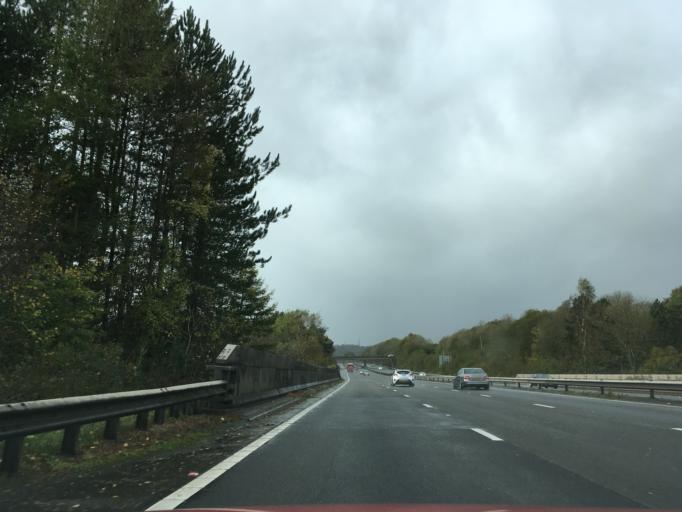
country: GB
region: Wales
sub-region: Caerphilly County Borough
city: Caerphilly
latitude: 51.5465
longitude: -3.1840
